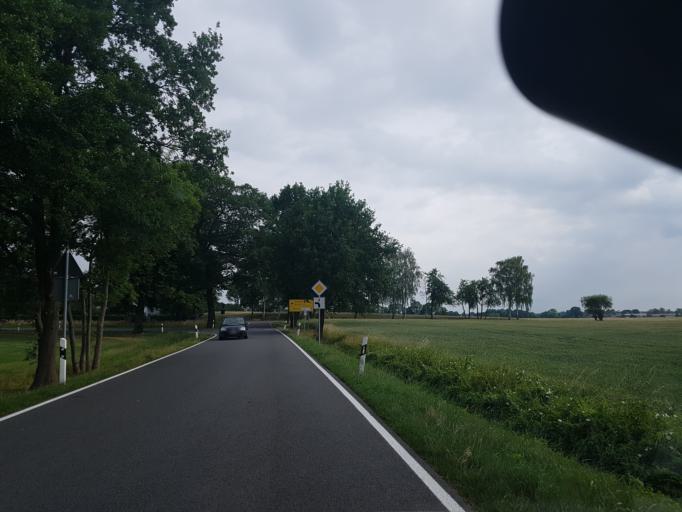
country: DE
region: Brandenburg
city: Sonnewalde
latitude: 51.7001
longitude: 13.6219
